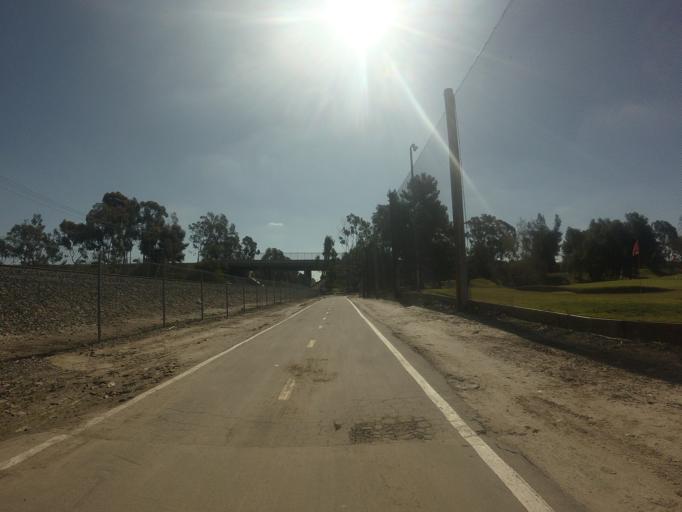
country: US
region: California
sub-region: Orange County
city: Lake Forest
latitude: 33.6215
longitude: -117.6886
